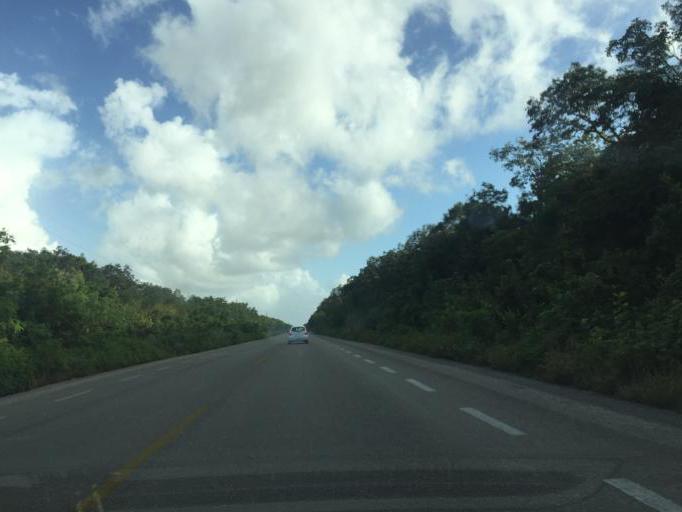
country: MX
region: Quintana Roo
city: Coba
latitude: 20.4596
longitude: -87.6775
